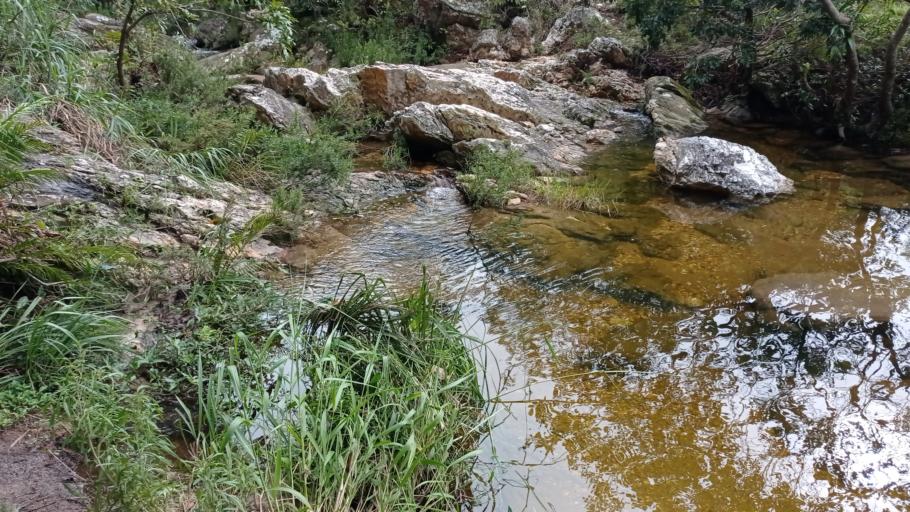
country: BR
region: Minas Gerais
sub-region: Sao Joao Del Rei
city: Sao Joao del Rei
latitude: -21.1256
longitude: -44.2725
